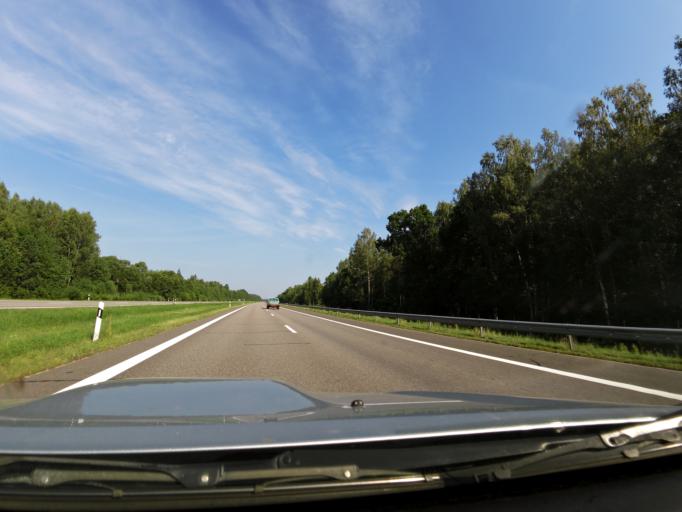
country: LT
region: Panevezys
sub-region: Panevezys City
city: Panevezys
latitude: 55.6254
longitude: 24.4069
